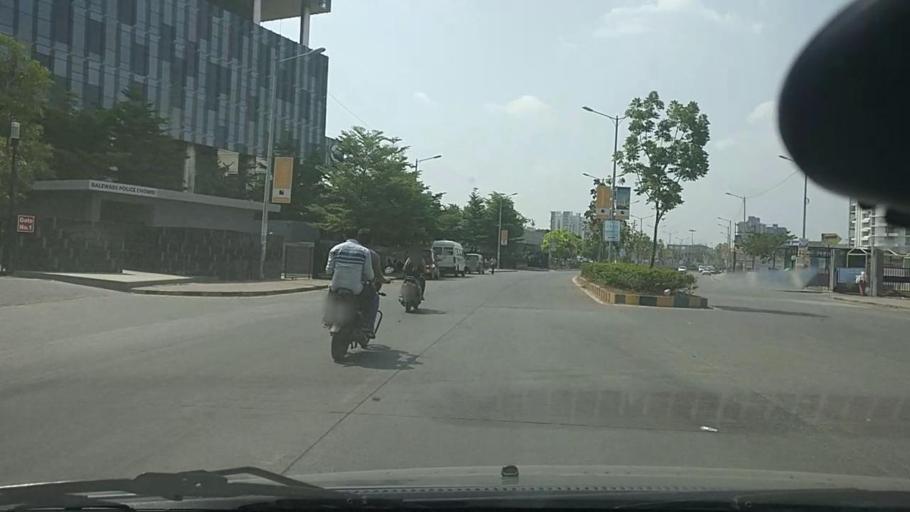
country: IN
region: Maharashtra
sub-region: Pune Division
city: Pimpri
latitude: 18.5684
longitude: 73.7753
